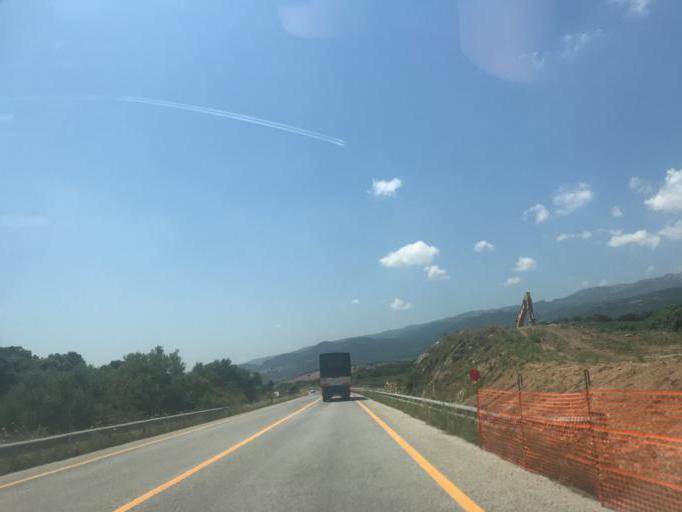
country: IT
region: Sardinia
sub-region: Provincia di Olbia-Tempio
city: Berchidda
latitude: 40.7808
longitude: 9.2239
